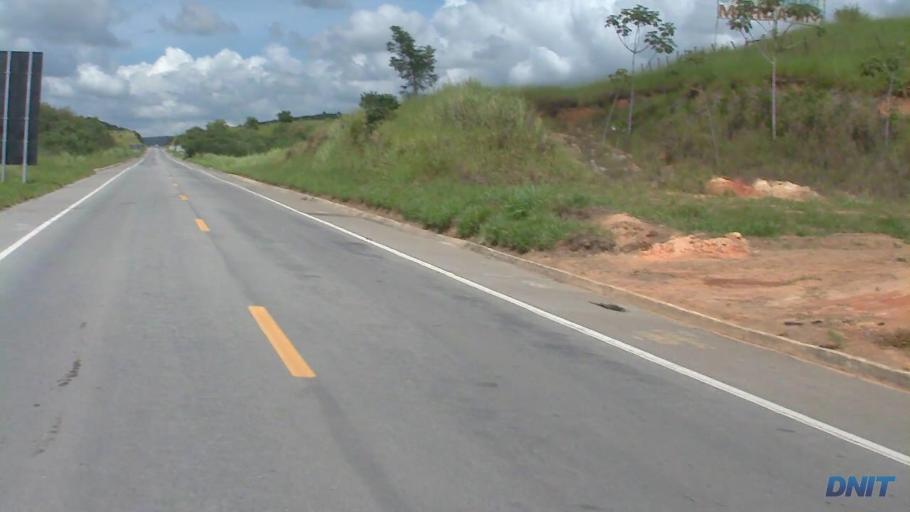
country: BR
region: Minas Gerais
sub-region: Governador Valadares
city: Governador Valadares
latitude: -18.9933
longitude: -42.1171
